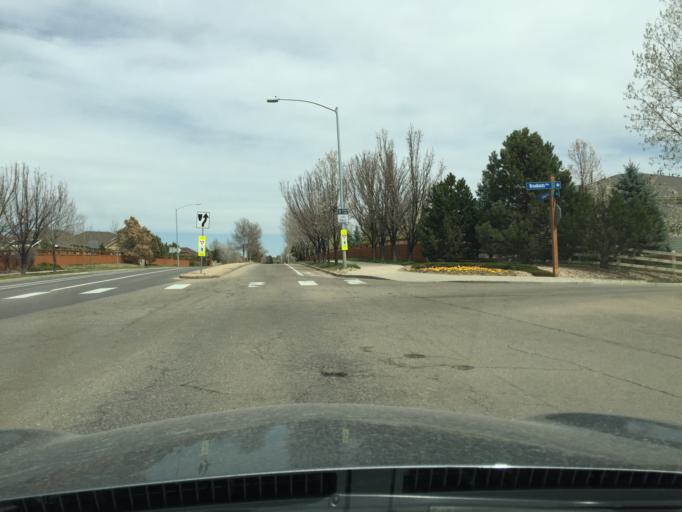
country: US
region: Colorado
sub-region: Broomfield County
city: Broomfield
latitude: 39.9522
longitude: -105.0344
